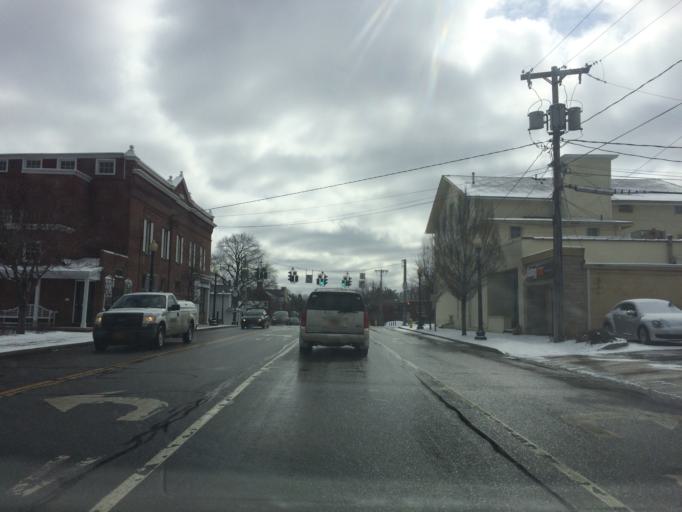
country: US
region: New York
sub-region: Monroe County
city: Pittsford
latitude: 43.0911
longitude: -77.5161
